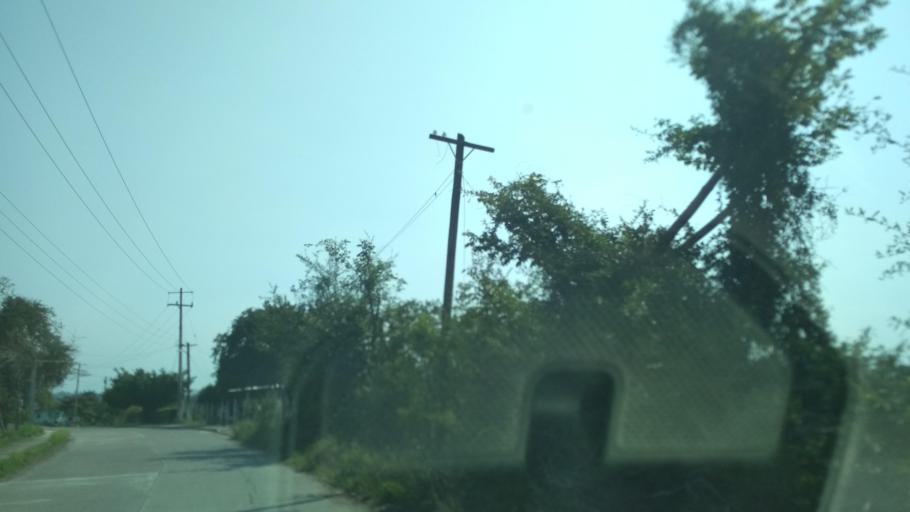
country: MX
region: Veracruz
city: Gutierrez Zamora
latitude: 20.4152
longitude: -97.1874
